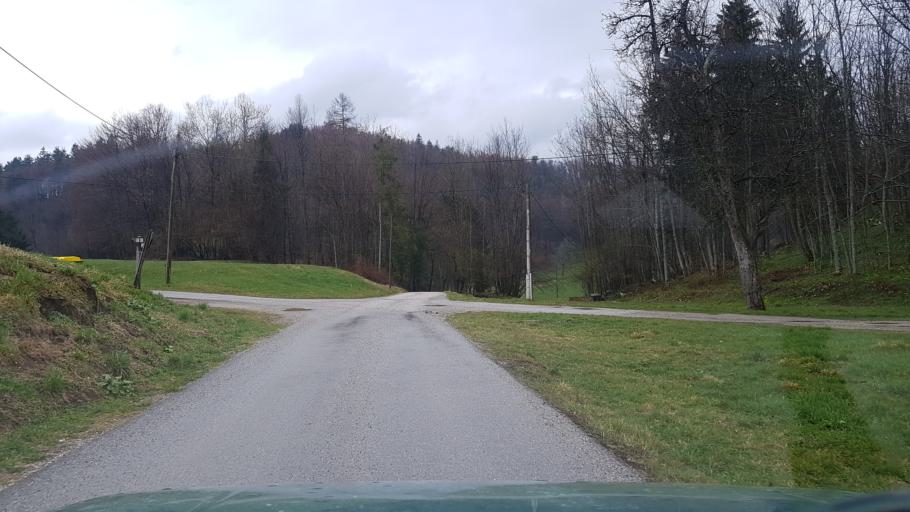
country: SI
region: Tolmin
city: Tolmin
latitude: 46.1402
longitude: 13.8388
